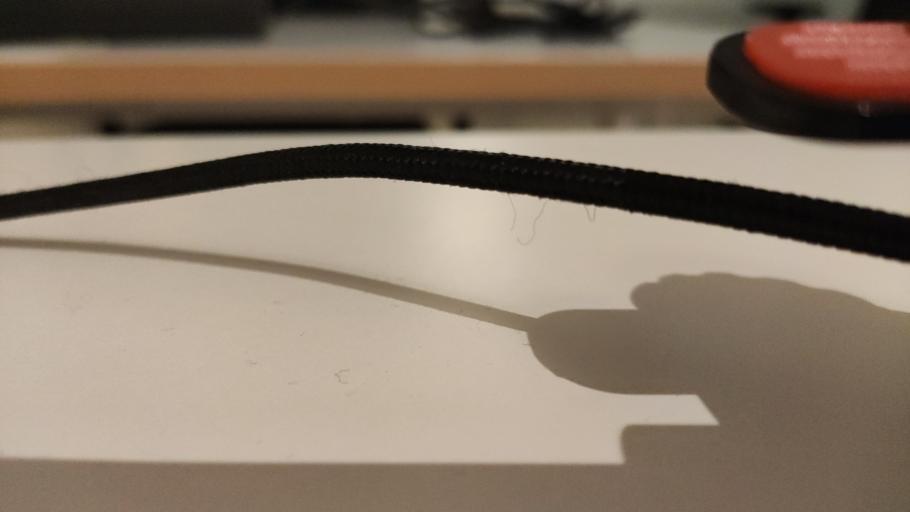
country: RU
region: Moskovskaya
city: Elektrogorsk
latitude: 55.9878
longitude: 38.7813
